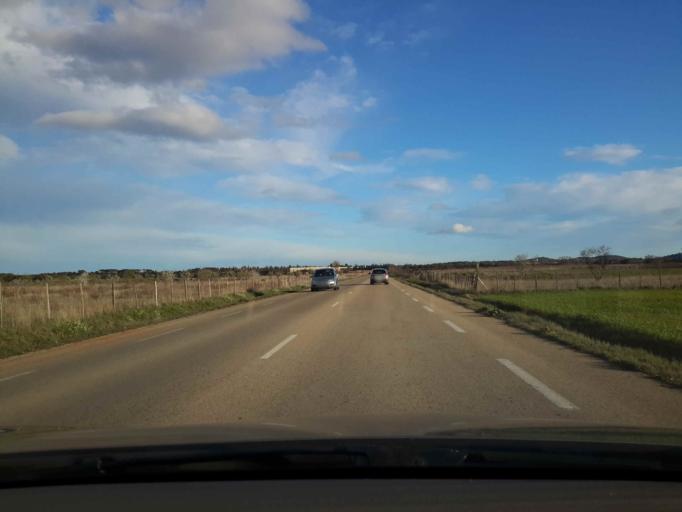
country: FR
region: Languedoc-Roussillon
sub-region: Departement du Gard
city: Aubord
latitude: 43.7660
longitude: 4.3301
